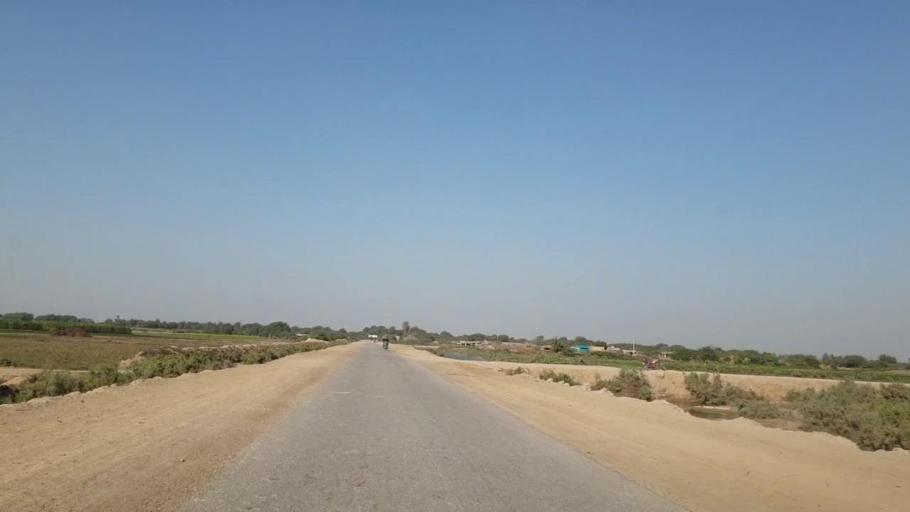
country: PK
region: Sindh
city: Digri
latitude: 25.1178
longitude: 69.1080
